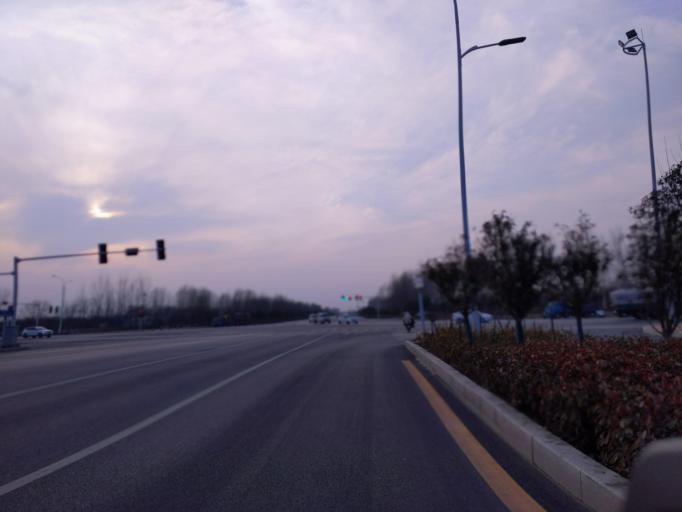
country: CN
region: Henan Sheng
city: Puyang
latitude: 35.8193
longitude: 114.9937
